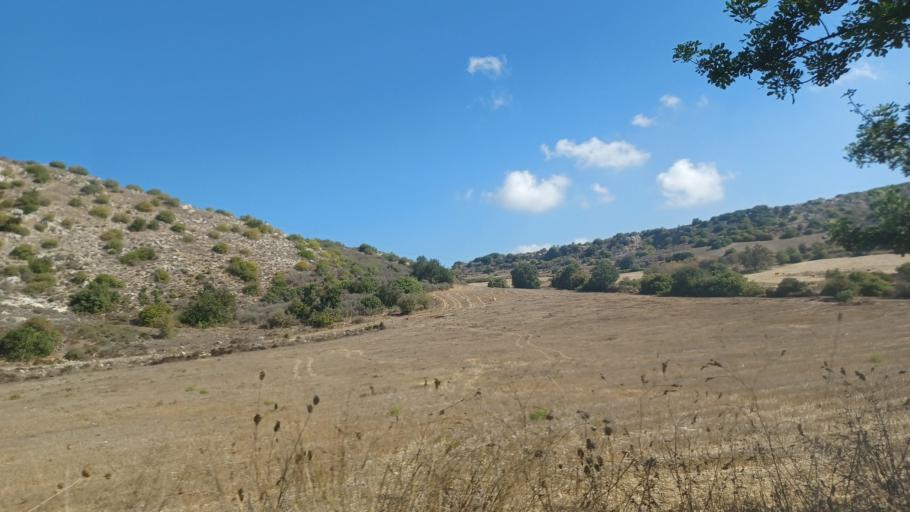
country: CY
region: Pafos
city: Polis
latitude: 34.9819
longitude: 32.4958
